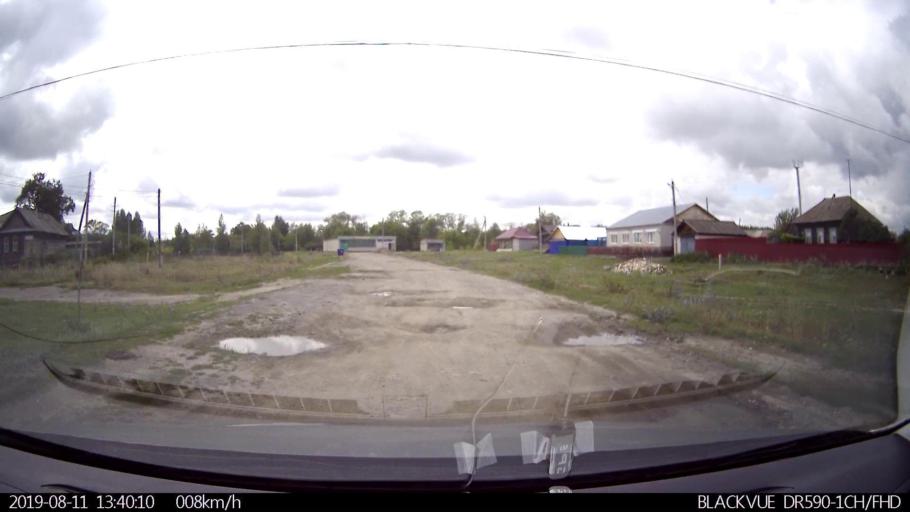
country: RU
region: Ulyanovsk
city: Ignatovka
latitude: 53.8589
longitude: 47.5782
